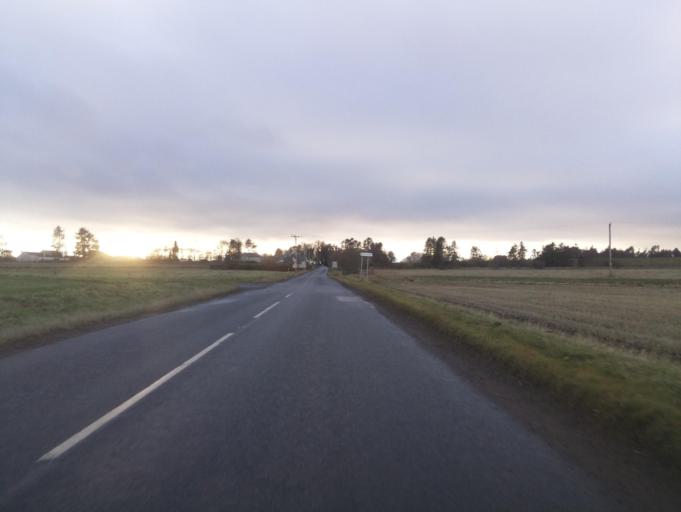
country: GB
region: Scotland
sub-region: Angus
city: Letham
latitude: 56.5364
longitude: -2.7919
